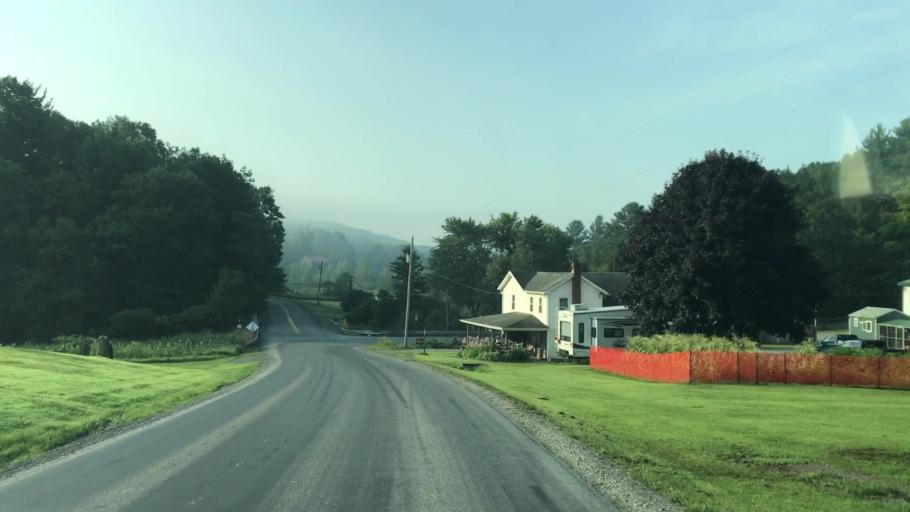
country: US
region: Pennsylvania
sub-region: Wyoming County
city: Factoryville
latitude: 41.6512
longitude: -75.7973
